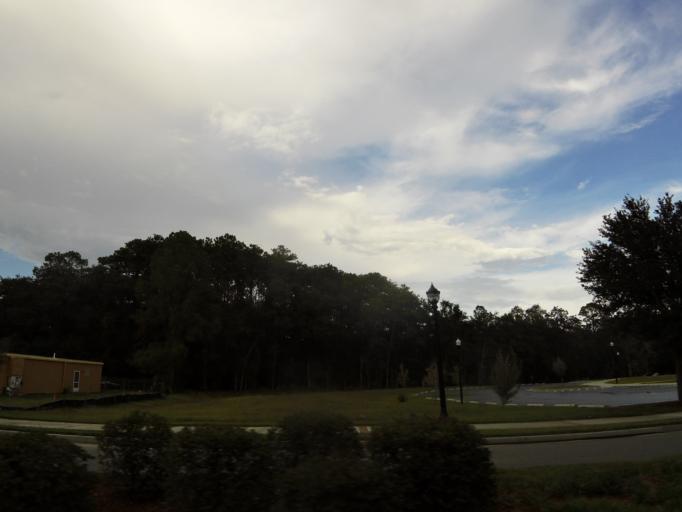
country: US
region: Georgia
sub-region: Liberty County
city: Hinesville
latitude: 31.8514
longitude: -81.5999
